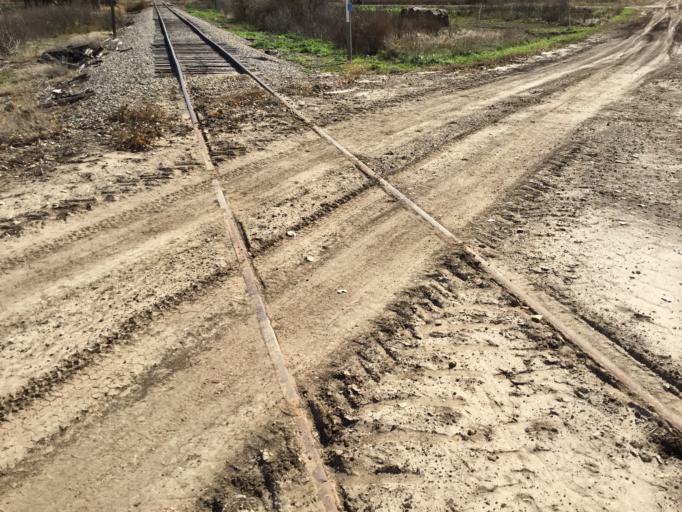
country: US
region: Kansas
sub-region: Lincoln County
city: Lincoln
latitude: 38.9158
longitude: -98.0032
